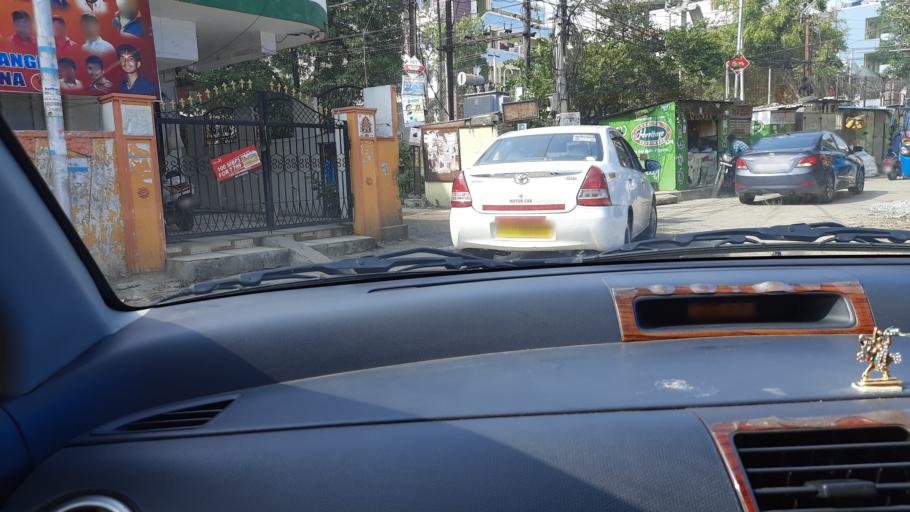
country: IN
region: Telangana
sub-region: Rangareddi
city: Quthbullapur
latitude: 17.4474
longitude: 78.4589
